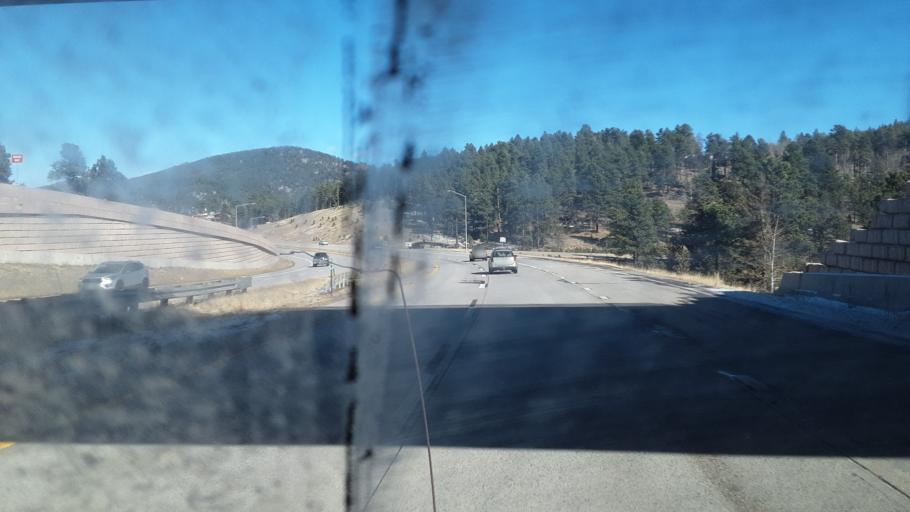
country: US
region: Colorado
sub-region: Jefferson County
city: Evergreen
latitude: 39.5299
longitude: -105.3061
